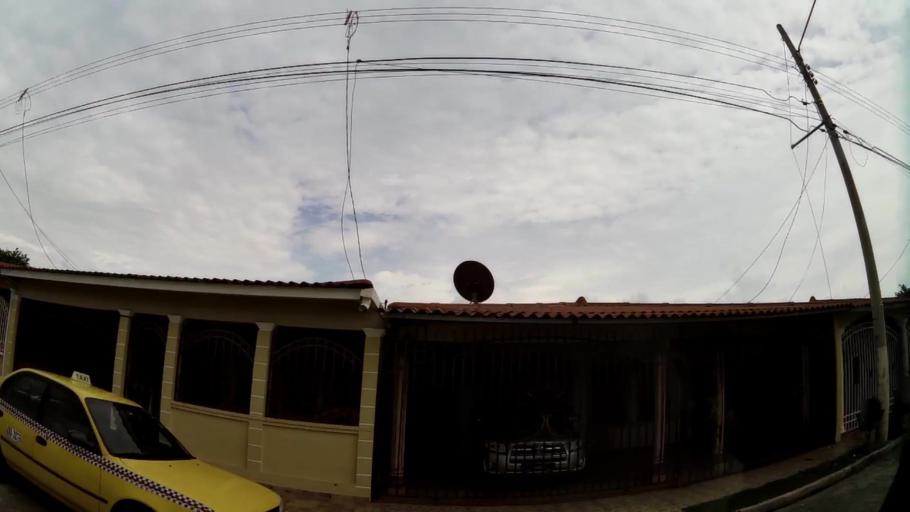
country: PA
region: Panama
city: Tocumen
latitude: 9.0462
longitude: -79.4017
